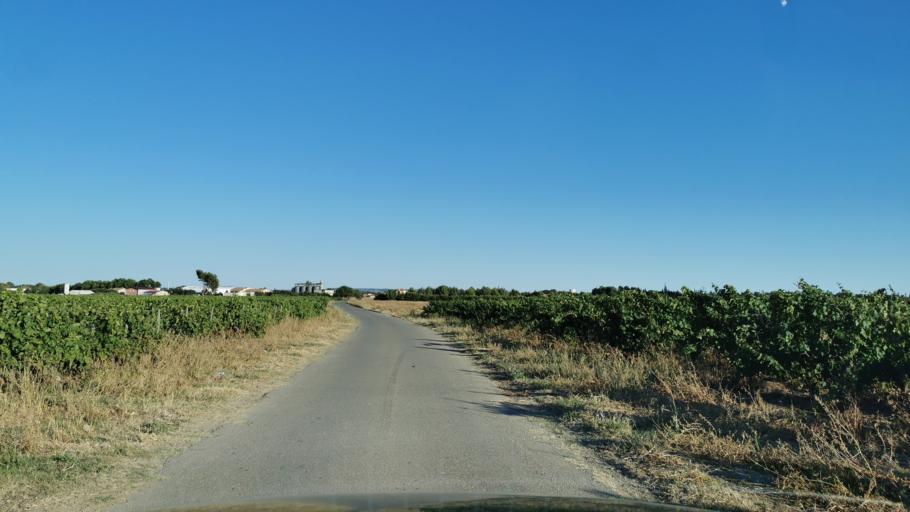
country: FR
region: Languedoc-Roussillon
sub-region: Departement de l'Aude
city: Ouveillan
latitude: 43.2566
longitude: 2.9900
